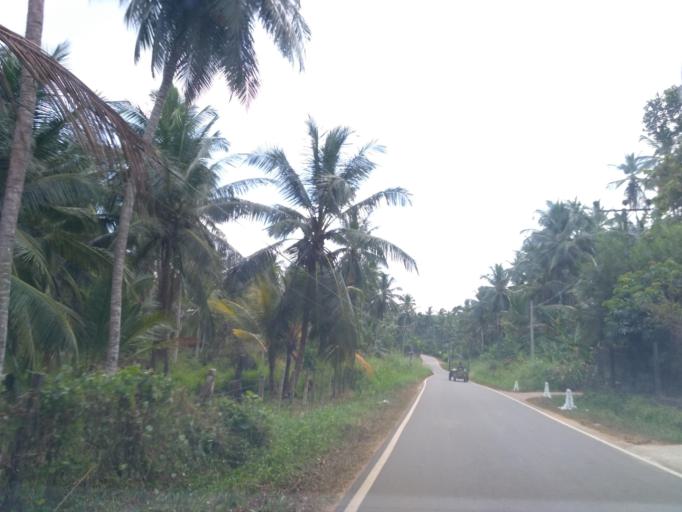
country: LK
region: North Western
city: Kuliyapitiya
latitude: 7.3364
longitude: 80.0617
